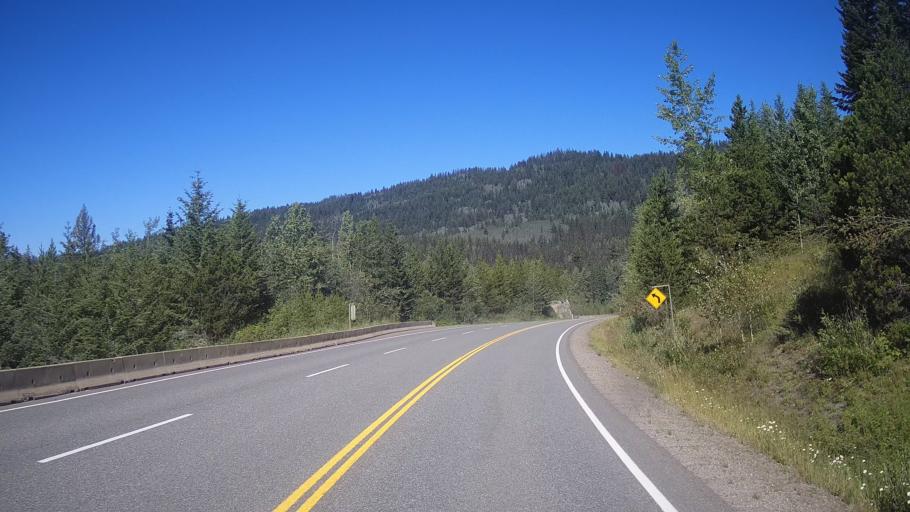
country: CA
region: British Columbia
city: Kamloops
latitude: 51.4763
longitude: -120.4801
